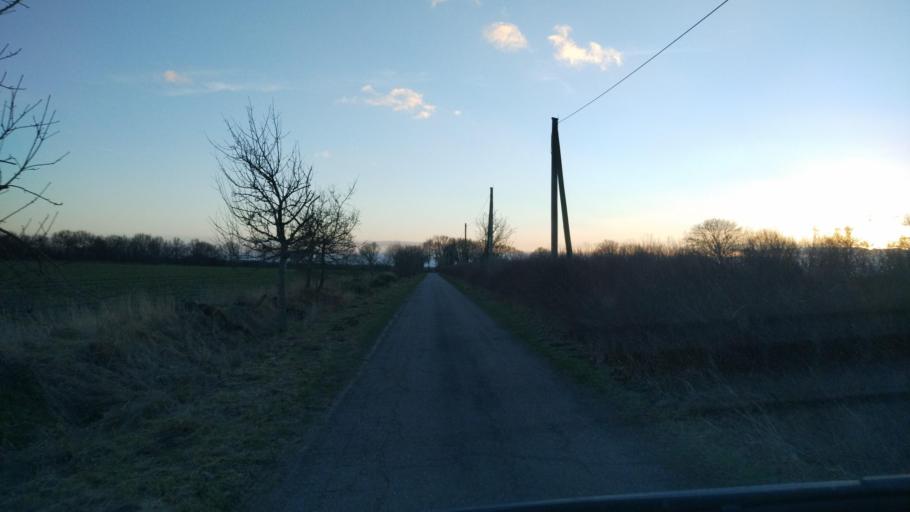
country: DE
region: Schleswig-Holstein
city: Gross Rheide
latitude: 54.4454
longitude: 9.4118
